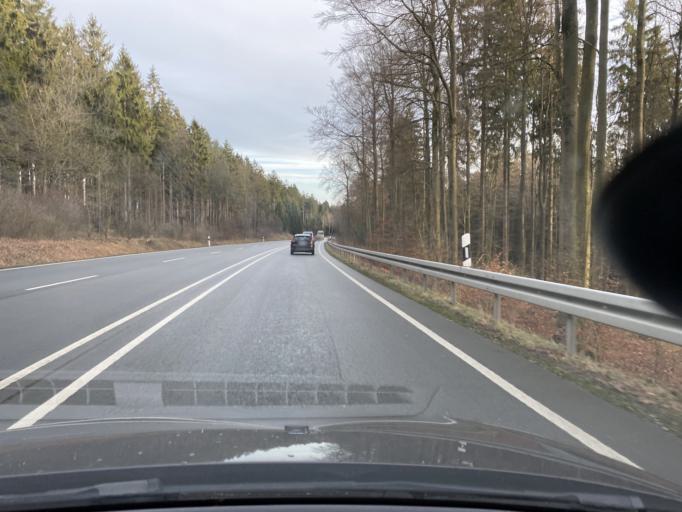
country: DE
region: North Rhine-Westphalia
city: Warstein
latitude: 51.4054
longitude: 8.3173
